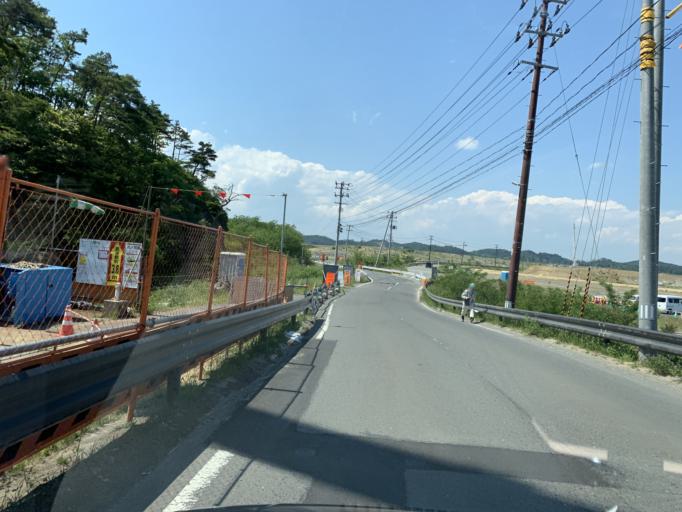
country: JP
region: Miyagi
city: Yamoto
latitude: 38.3545
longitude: 141.1568
